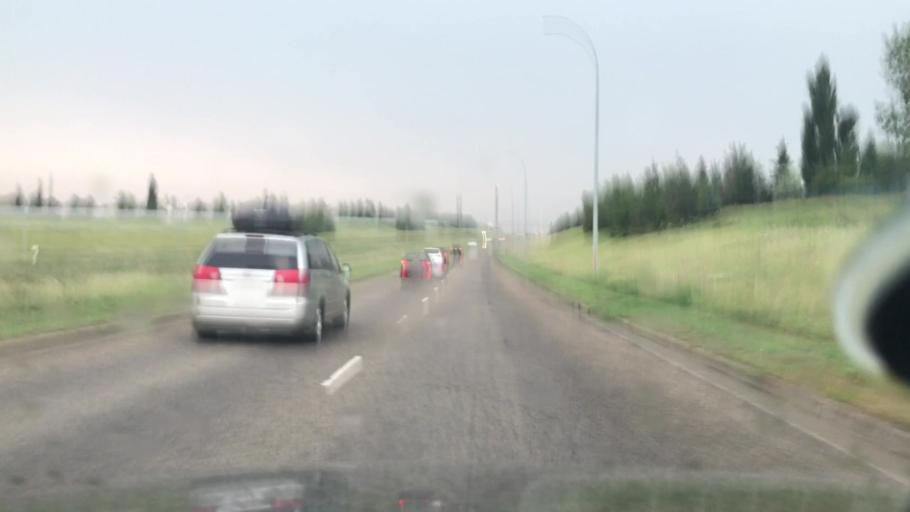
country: CA
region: Alberta
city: Edmonton
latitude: 53.4676
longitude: -113.5836
